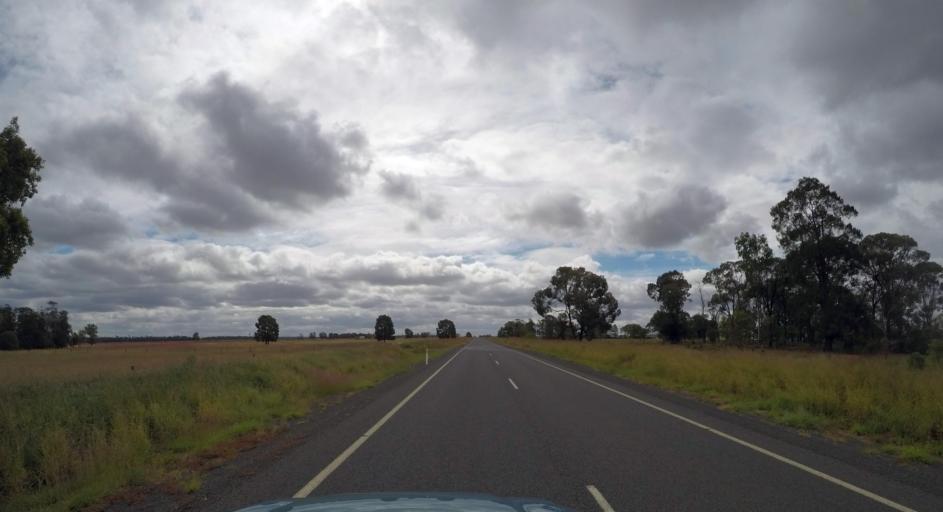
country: AU
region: Queensland
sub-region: South Burnett
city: Kingaroy
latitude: -26.3838
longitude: 151.2454
